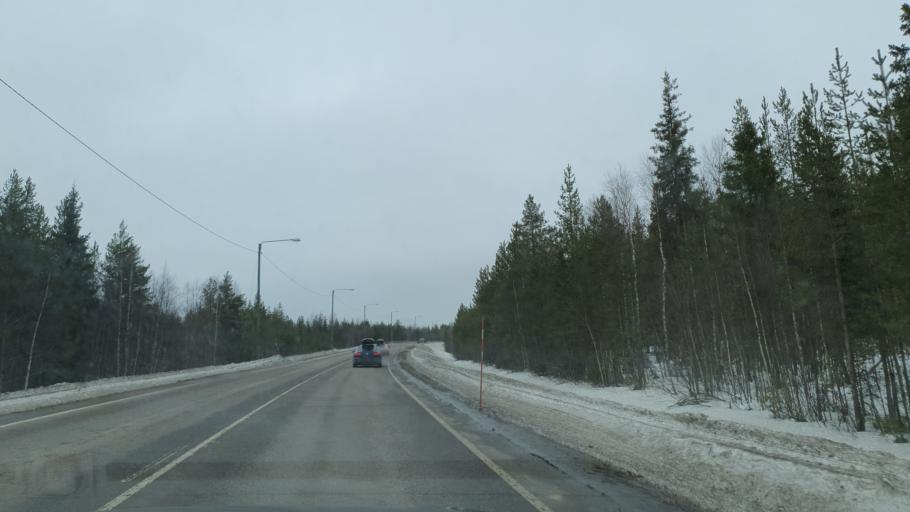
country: FI
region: Lapland
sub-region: Torniolaakso
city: Pello
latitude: 66.8278
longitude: 24.0014
